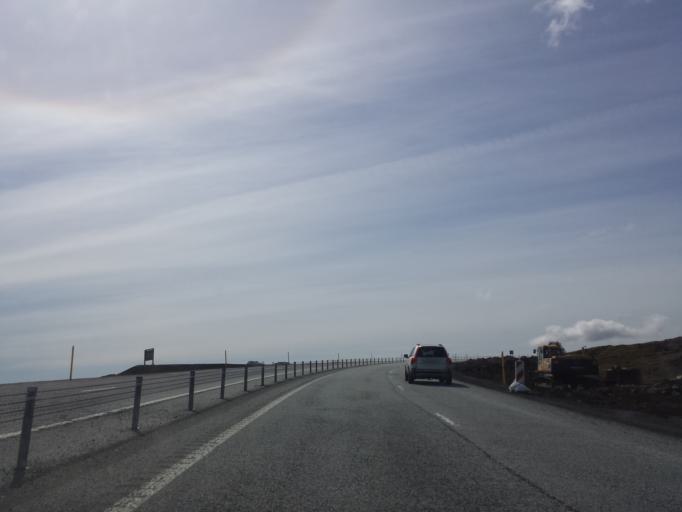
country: IS
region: South
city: Hveragerdi
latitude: 64.0133
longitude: -21.2338
